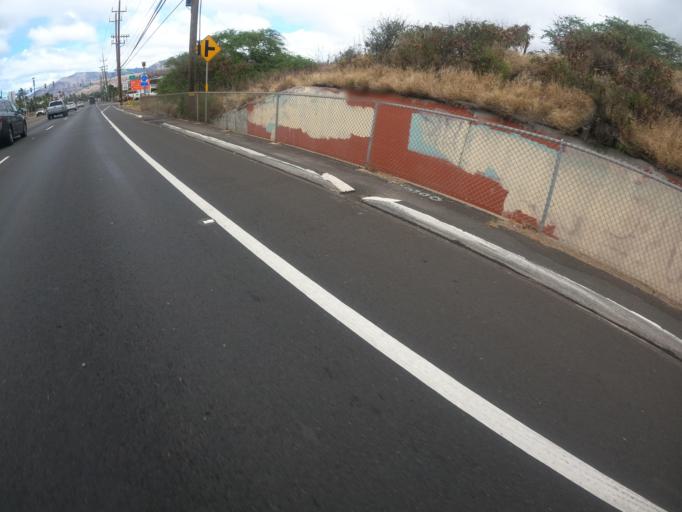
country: US
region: Hawaii
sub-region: Honolulu County
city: Ma'ili
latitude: 21.4032
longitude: -158.1765
